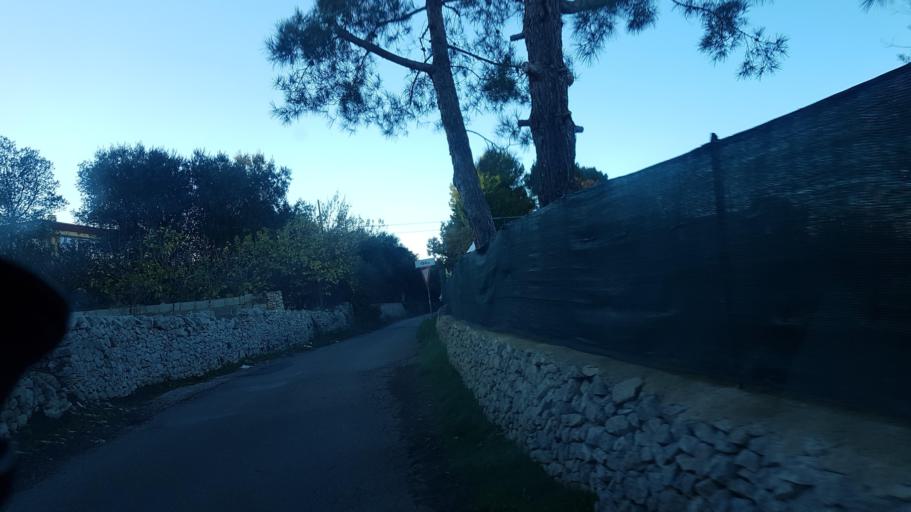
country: IT
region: Apulia
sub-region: Provincia di Brindisi
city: Ostuni
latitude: 40.7053
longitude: 17.5344
